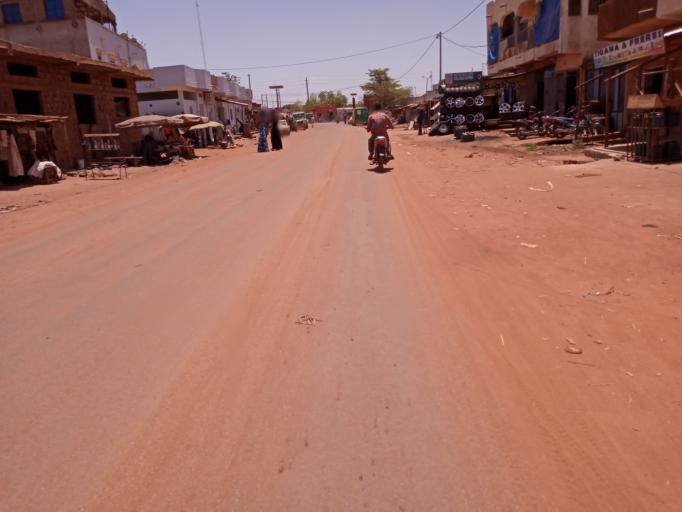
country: ML
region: Bamako
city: Bamako
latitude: 12.5743
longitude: -7.9700
